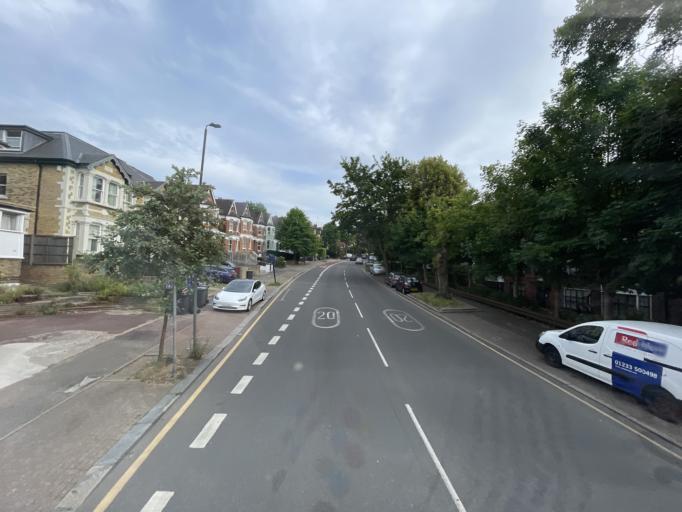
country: GB
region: England
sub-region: Greater London
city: Crouch End
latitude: 51.5980
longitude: -0.1460
